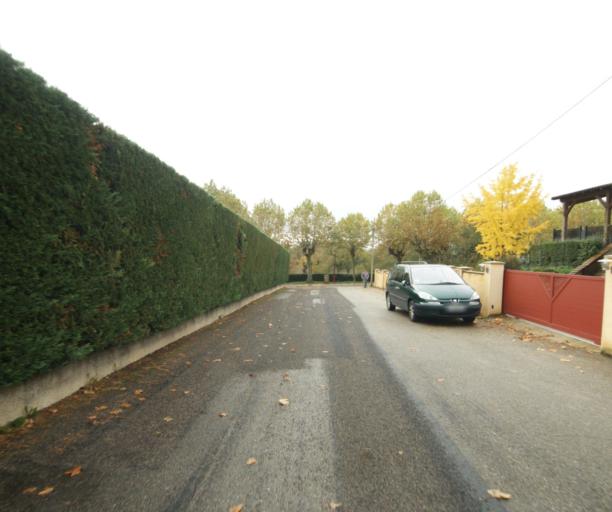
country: FR
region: Rhone-Alpes
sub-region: Departement de l'Ain
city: Pont-de-Vaux
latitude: 46.4762
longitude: 4.8734
